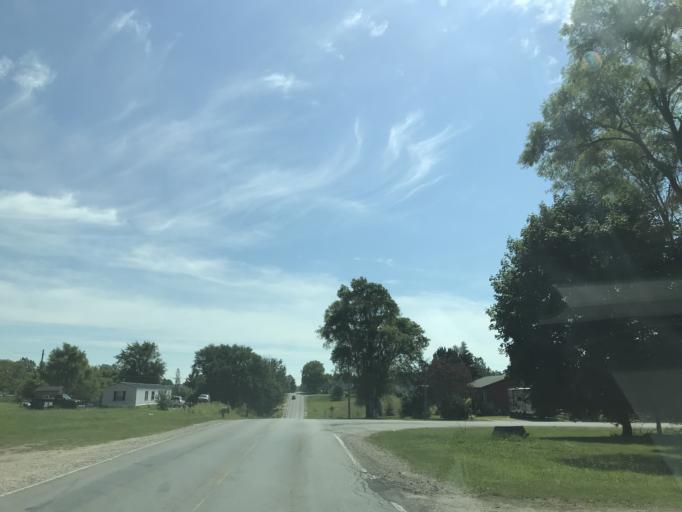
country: US
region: Michigan
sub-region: Grand Traverse County
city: Traverse City
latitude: 44.6575
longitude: -85.6655
